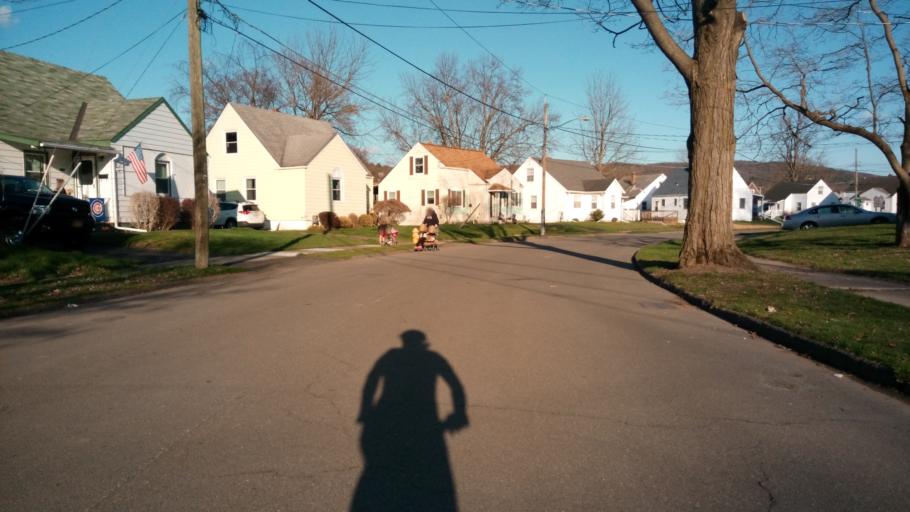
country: US
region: New York
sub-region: Chemung County
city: Elmira
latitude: 42.0791
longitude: -76.7864
